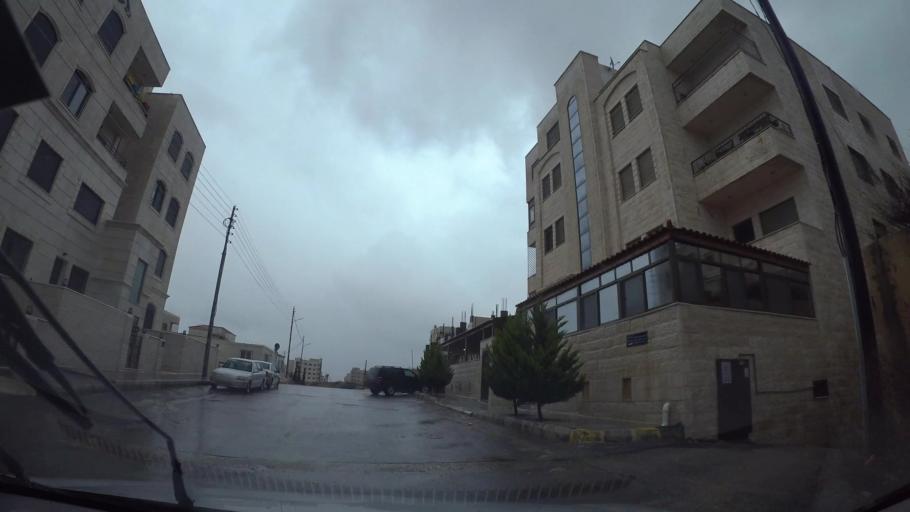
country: JO
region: Amman
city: Al Jubayhah
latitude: 32.0383
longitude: 35.8816
